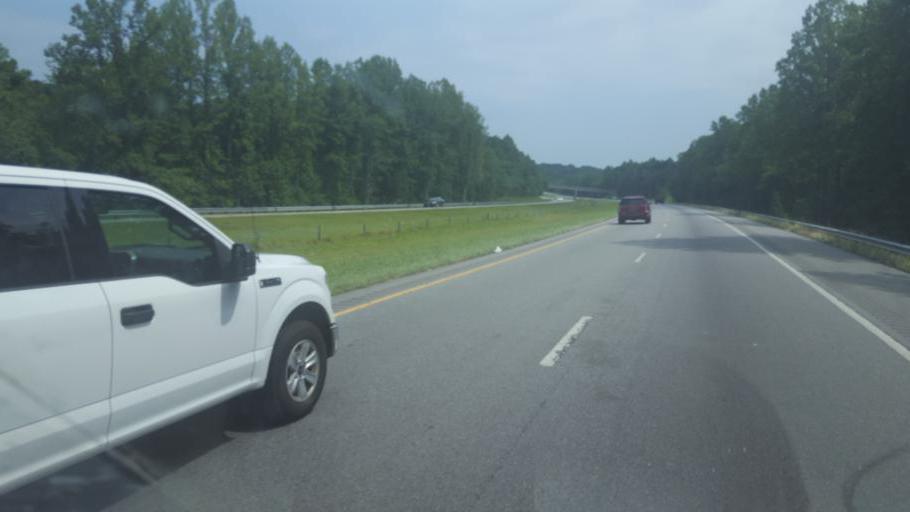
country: US
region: North Carolina
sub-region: Yadkin County
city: Yadkinville
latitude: 36.0242
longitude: -80.8225
